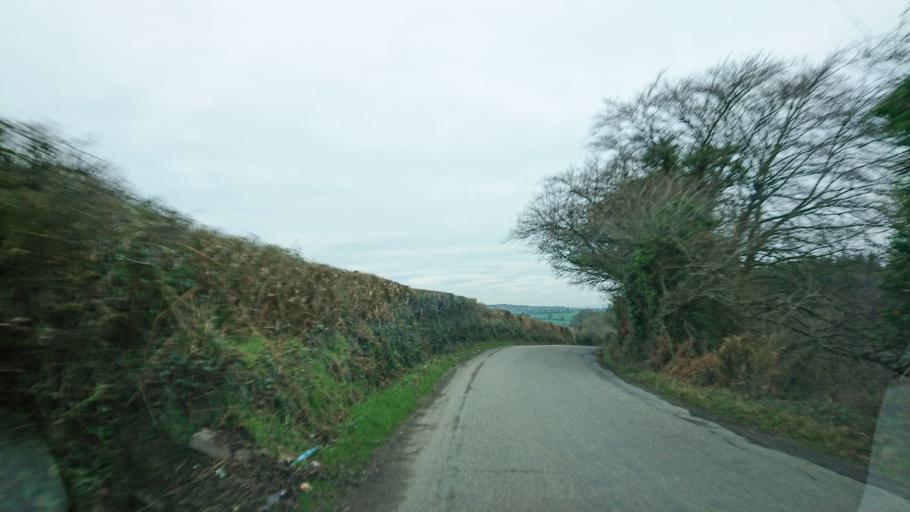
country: IE
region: Munster
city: Carrick-on-Suir
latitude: 52.2742
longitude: -7.4095
